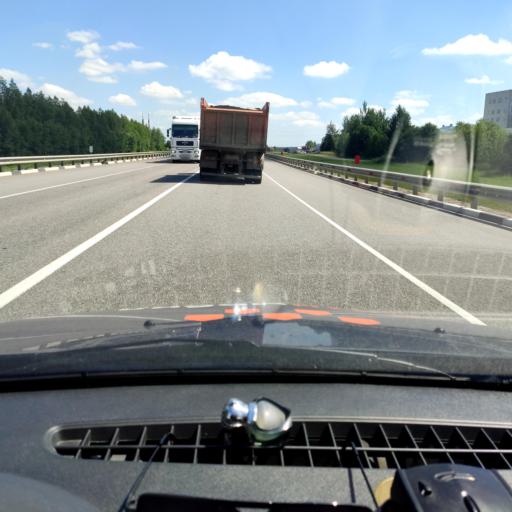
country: RU
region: Orjol
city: Orel
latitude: 52.8477
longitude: 36.2510
